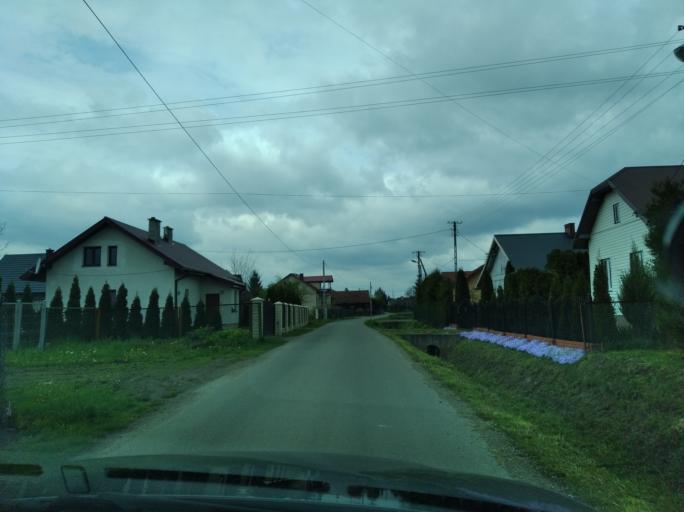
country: PL
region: Subcarpathian Voivodeship
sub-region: Powiat brzozowski
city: Turze Pole
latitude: 49.6232
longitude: 22.0031
